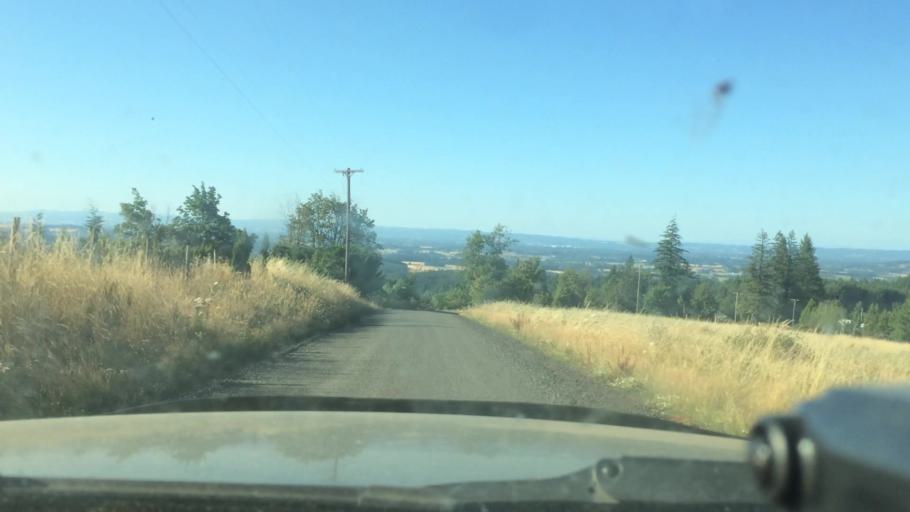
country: US
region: Oregon
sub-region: Yamhill County
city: Newberg
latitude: 45.3654
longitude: -122.9821
